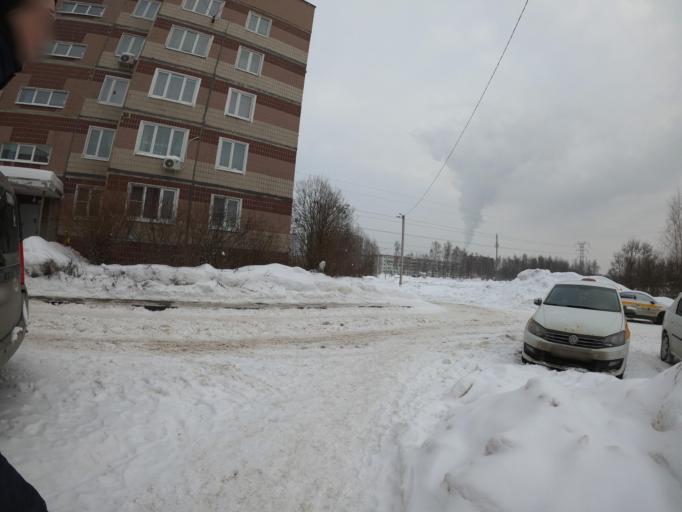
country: RU
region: Moskovskaya
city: Elektrogorsk
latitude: 55.8712
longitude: 38.7794
